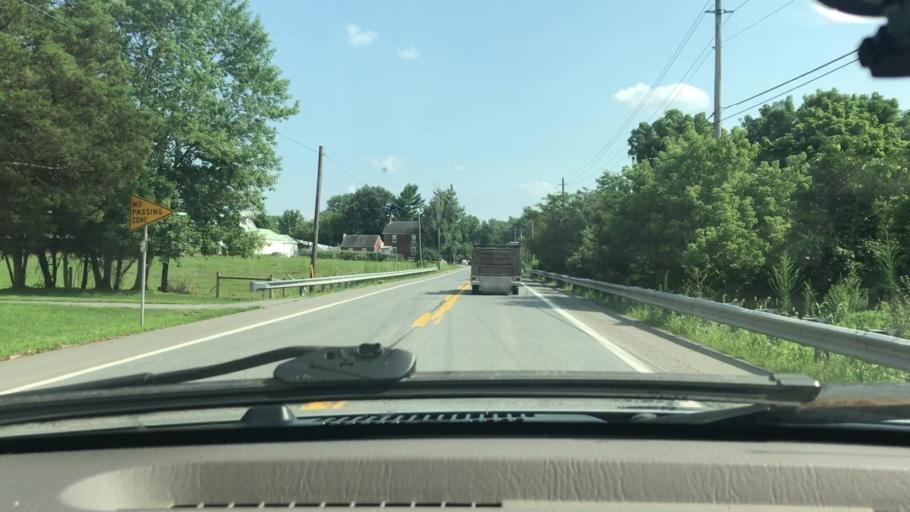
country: US
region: Pennsylvania
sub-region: Lancaster County
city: Elizabethtown
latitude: 40.2030
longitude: -76.6115
